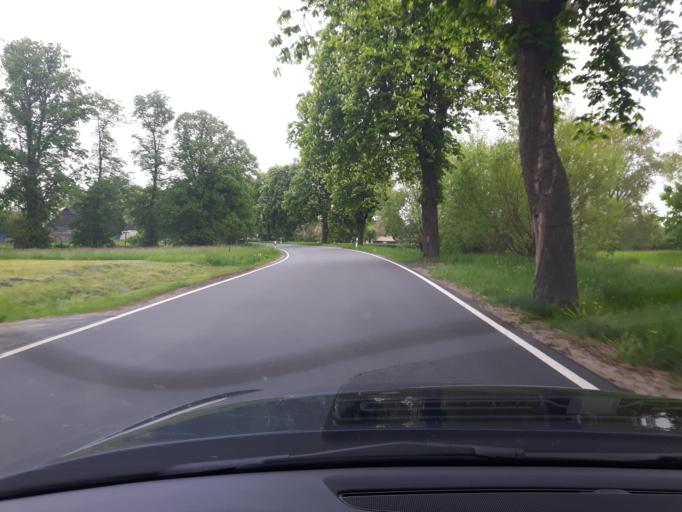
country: DE
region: Mecklenburg-Vorpommern
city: Gnoien
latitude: 54.0274
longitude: 12.6630
